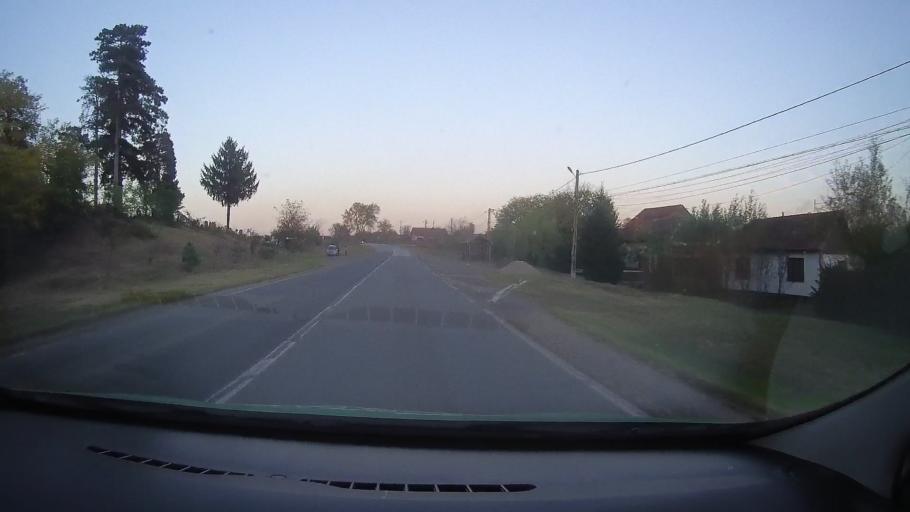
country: RO
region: Timis
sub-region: Comuna Dumbrava
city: Dumbrava
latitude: 45.8271
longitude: 22.1204
